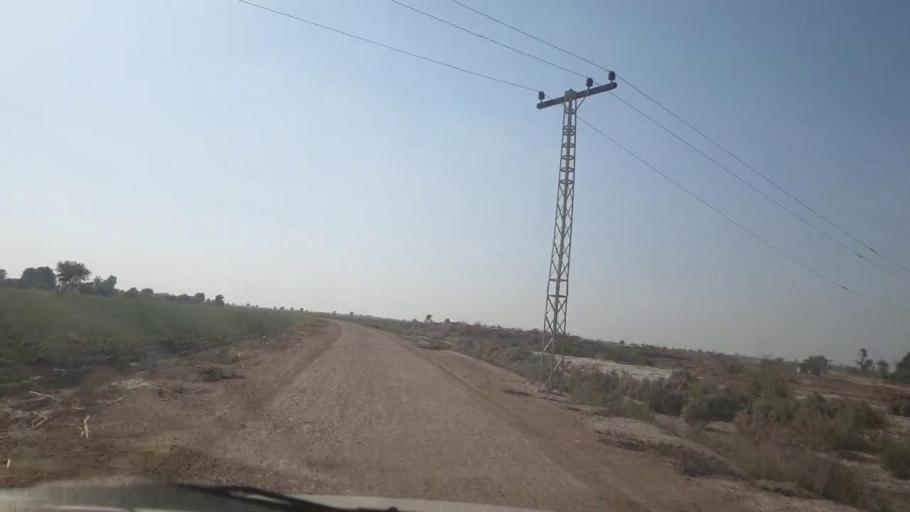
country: PK
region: Sindh
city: Mirpur Khas
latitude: 25.4551
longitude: 69.1219
